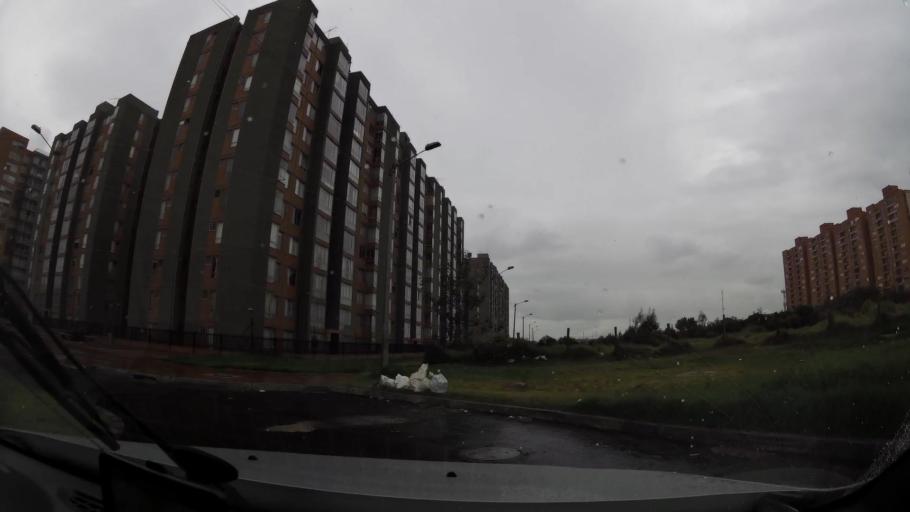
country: CO
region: Bogota D.C.
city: Bogota
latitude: 4.6582
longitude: -74.1294
